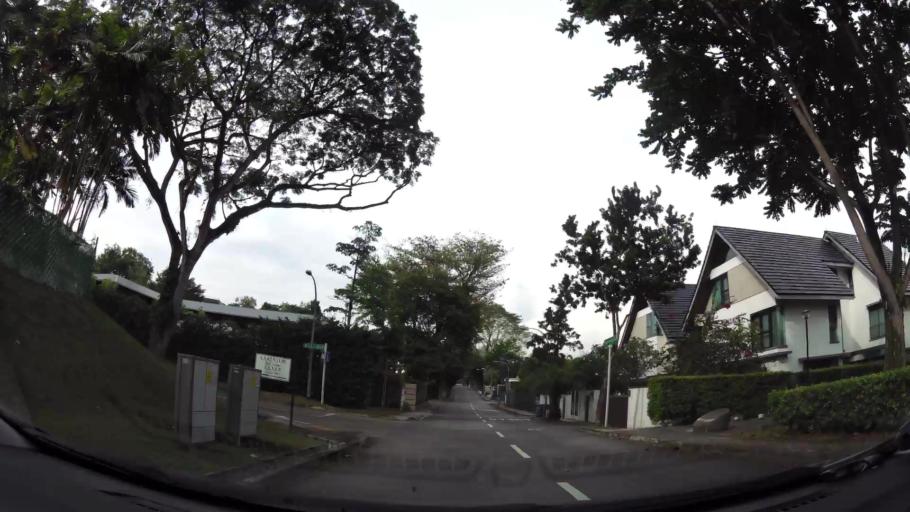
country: SG
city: Singapore
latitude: 1.3257
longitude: 103.8173
